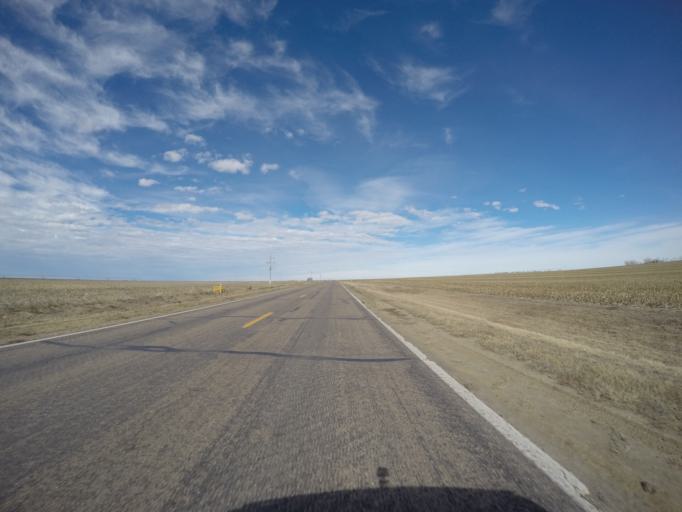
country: US
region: Nebraska
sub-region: Franklin County
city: Franklin
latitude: 40.2153
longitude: -98.9524
